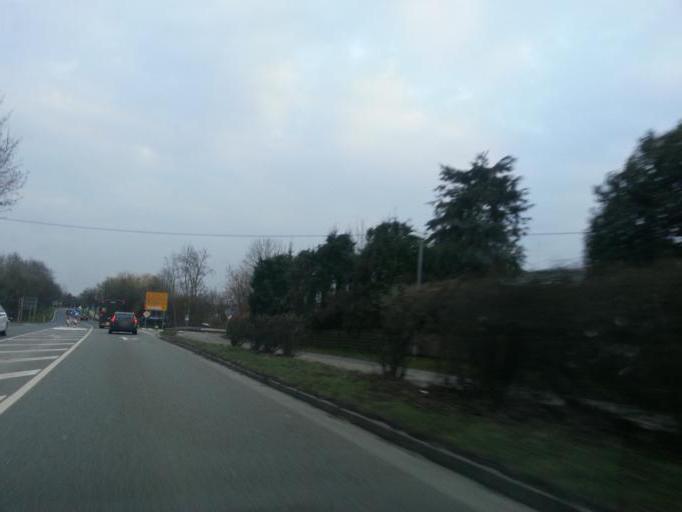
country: DE
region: Baden-Wuerttemberg
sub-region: Tuebingen Region
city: Markdorf
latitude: 47.7159
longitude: 9.4086
